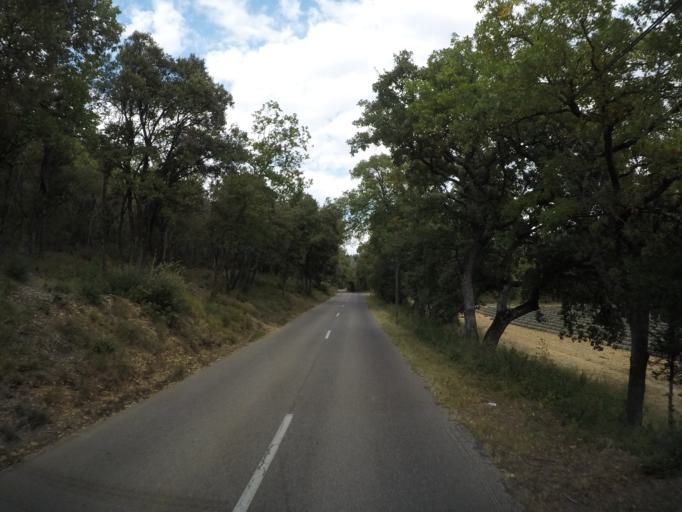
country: FR
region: Provence-Alpes-Cote d'Azur
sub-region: Departement des Alpes-de-Haute-Provence
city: Greoux-les-Bains
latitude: 43.7832
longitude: 5.9121
